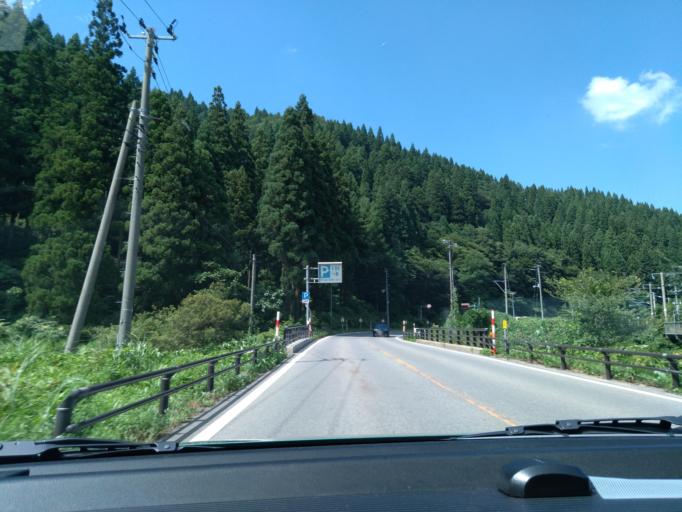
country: JP
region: Akita
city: Kakunodatemachi
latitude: 39.6415
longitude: 140.6606
